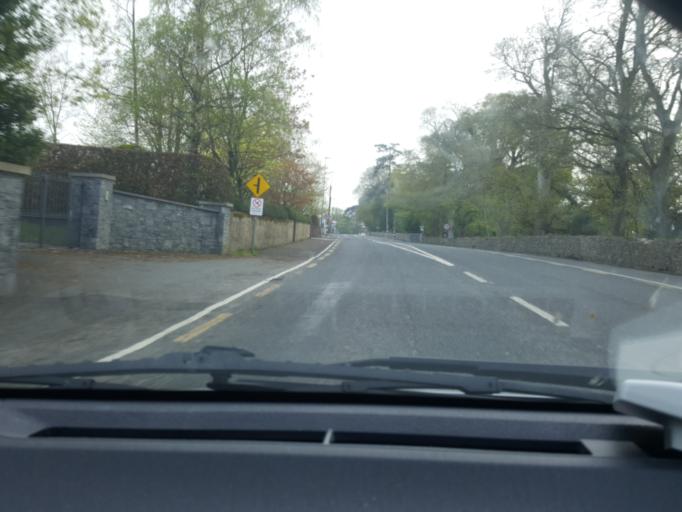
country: IE
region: Munster
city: Cahir
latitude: 52.3834
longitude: -7.9180
